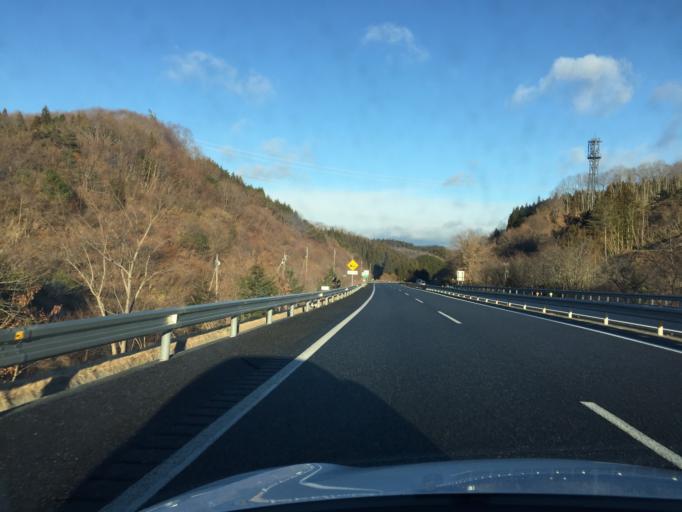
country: JP
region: Fukushima
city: Funehikimachi-funehiki
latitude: 37.2302
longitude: 140.6820
